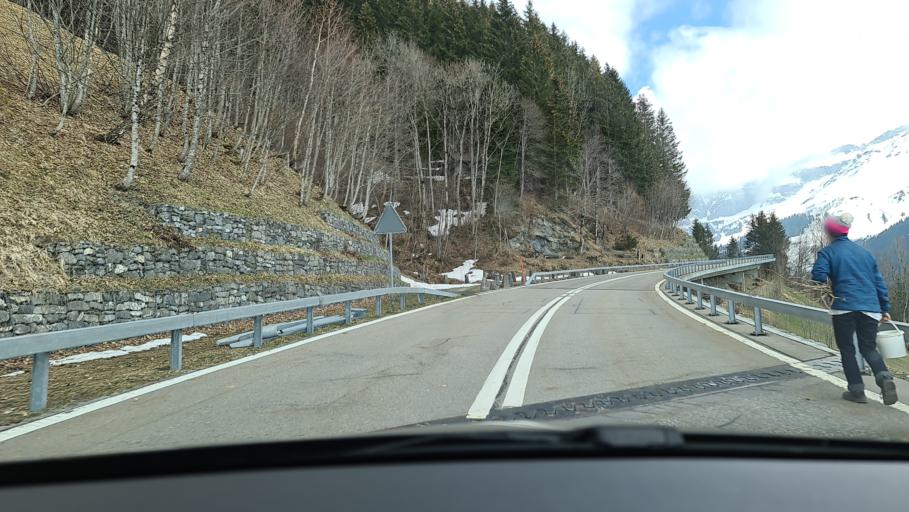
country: CH
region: Uri
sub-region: Uri
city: Burglen
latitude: 46.8710
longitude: 8.7680
